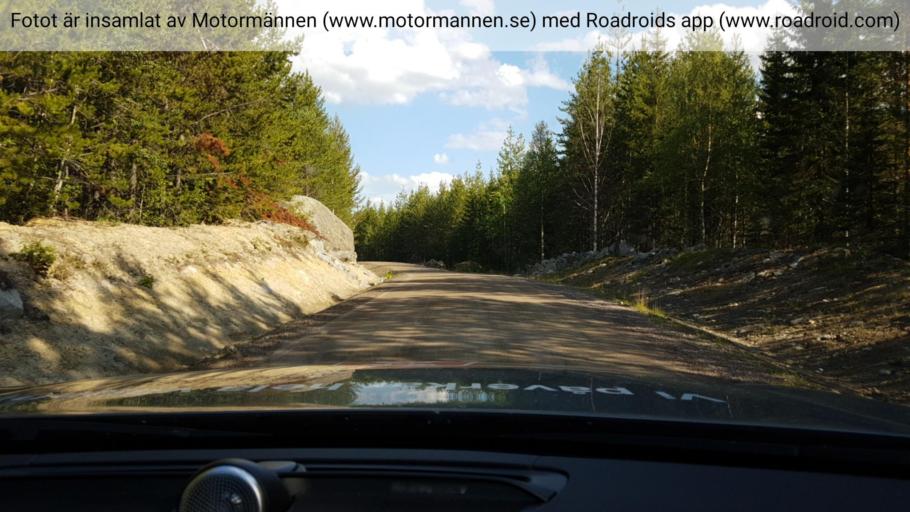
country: SE
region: Jaemtland
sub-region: Stroemsunds Kommun
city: Stroemsund
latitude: 63.9825
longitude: 16.0181
